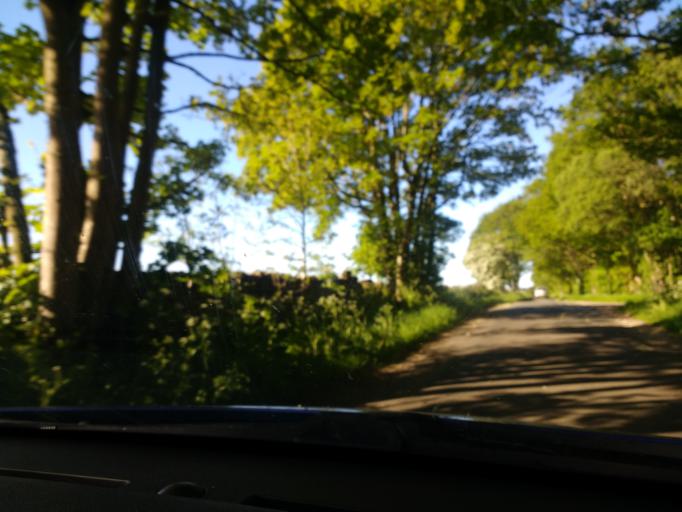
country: GB
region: England
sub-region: Cumbria
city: Appleby-in-Westmorland
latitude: 54.6673
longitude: -2.5974
